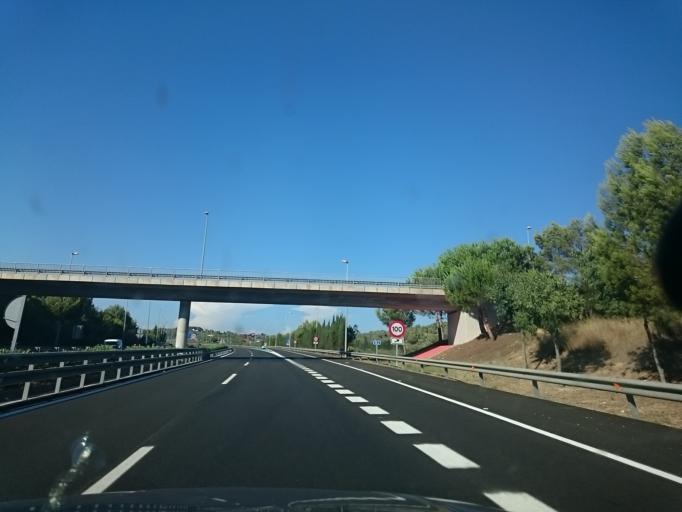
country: ES
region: Catalonia
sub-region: Provincia de Barcelona
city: Cubelles
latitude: 41.2171
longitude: 1.6726
